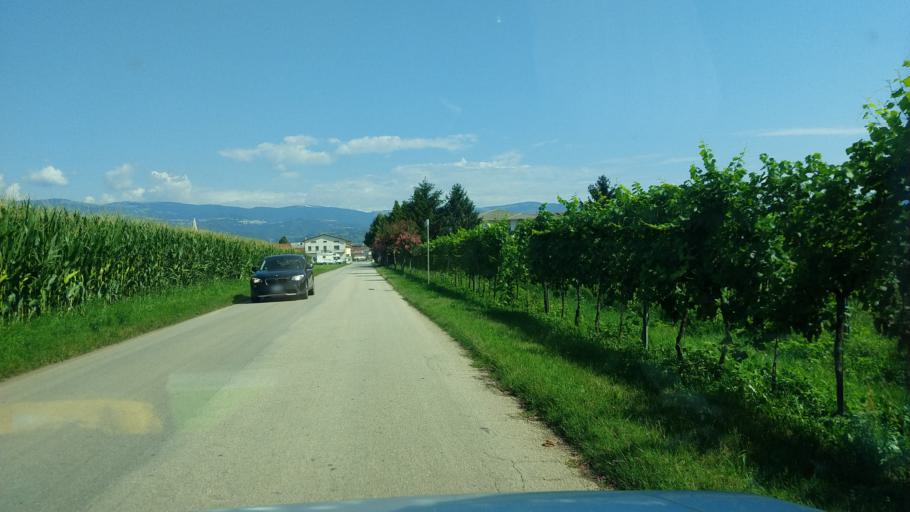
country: IT
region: Veneto
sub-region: Provincia di Vicenza
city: Sandrigo
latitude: 45.6819
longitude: 11.6061
